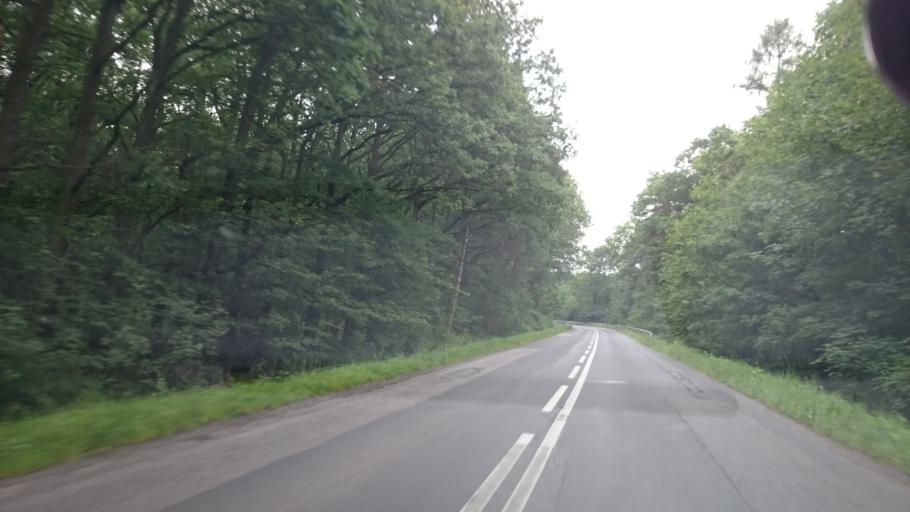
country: PL
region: Opole Voivodeship
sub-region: Powiat brzeski
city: Grodkow
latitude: 50.6651
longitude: 17.4203
